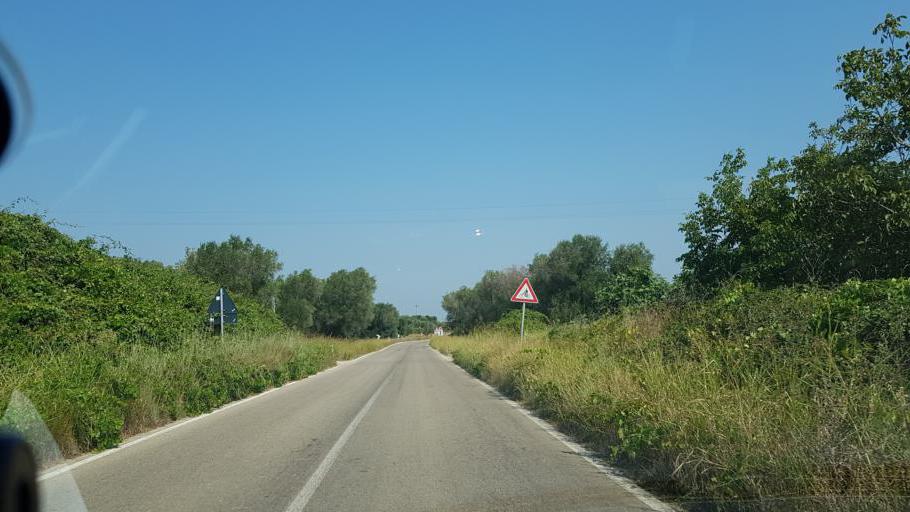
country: IT
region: Apulia
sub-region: Provincia di Brindisi
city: Torre Santa Susanna
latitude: 40.4989
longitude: 17.7304
